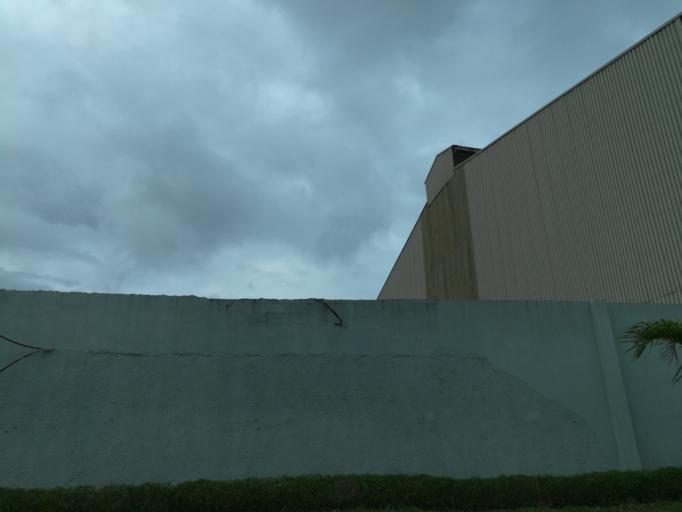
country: NG
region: Lagos
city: Ikeja
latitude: 6.5887
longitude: 3.3315
